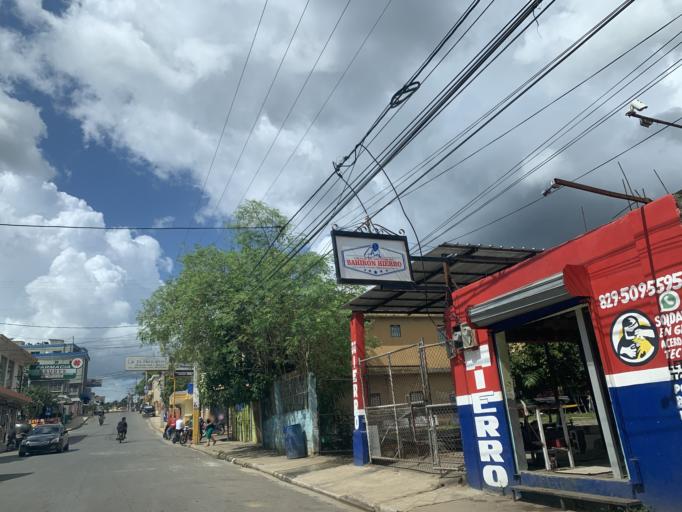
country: DO
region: Monte Plata
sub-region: Yamasa
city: Yamasa
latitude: 18.7662
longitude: -70.0222
